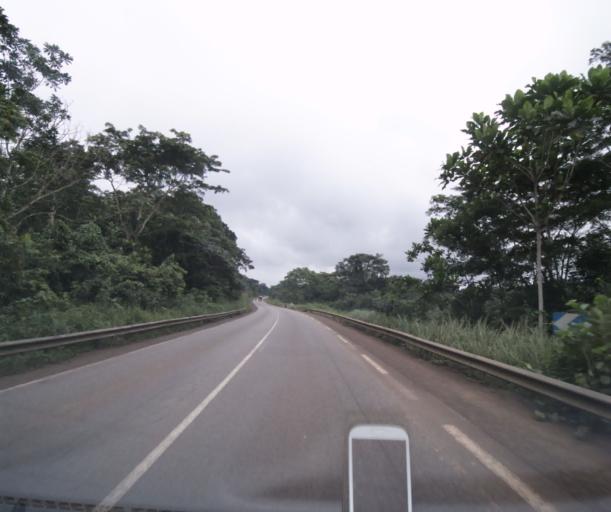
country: CM
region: Littoral
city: Edea
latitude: 3.8150
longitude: 10.3257
